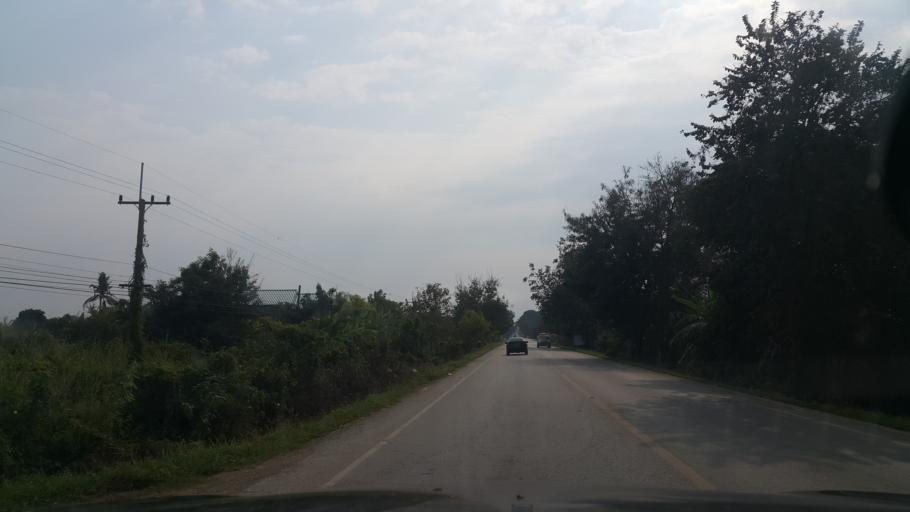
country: TH
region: Sukhothai
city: Si Samrong
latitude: 17.1807
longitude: 99.8378
